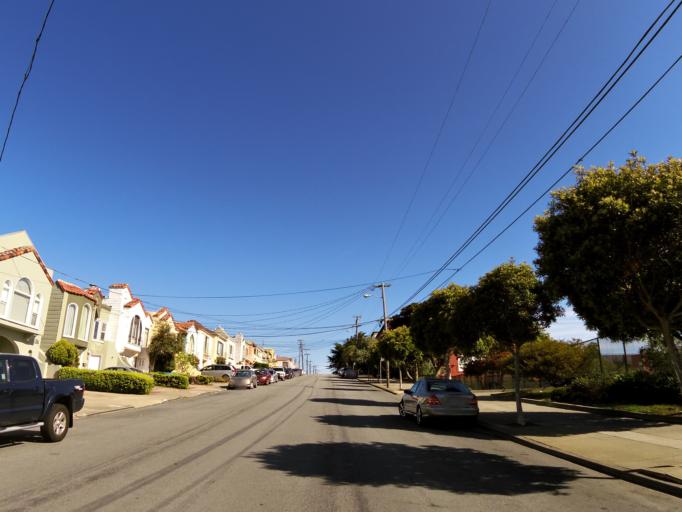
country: US
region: California
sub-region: San Mateo County
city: Daly City
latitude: 37.7453
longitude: -122.4812
